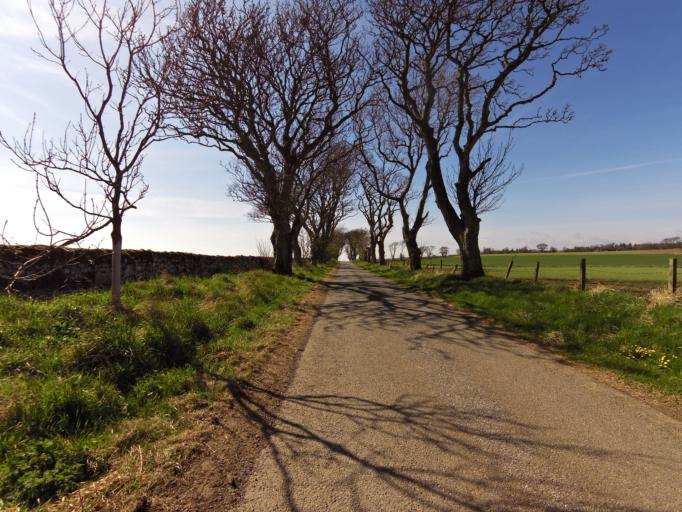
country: GB
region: Scotland
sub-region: Angus
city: Montrose
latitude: 56.6800
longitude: -2.4675
